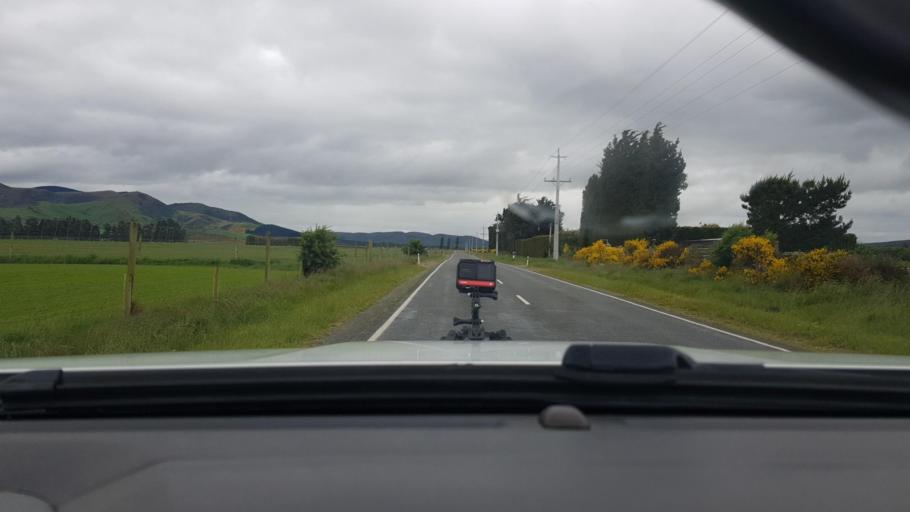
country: NZ
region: Southland
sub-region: Southland District
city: Winton
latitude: -45.8604
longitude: 168.3592
